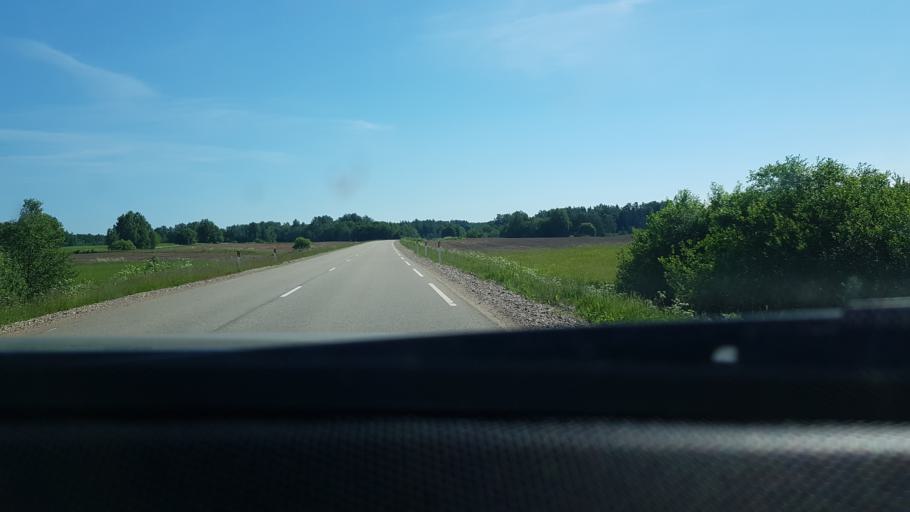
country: BY
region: Vitebsk
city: Braslaw
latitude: 55.8295
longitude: 26.9009
